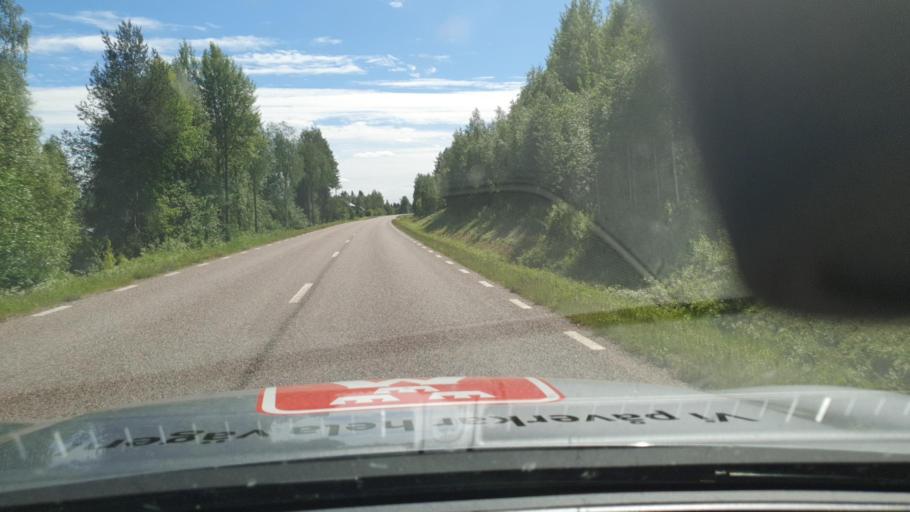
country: FI
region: Lapland
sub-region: Torniolaakso
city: Pello
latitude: 66.9484
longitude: 23.8487
